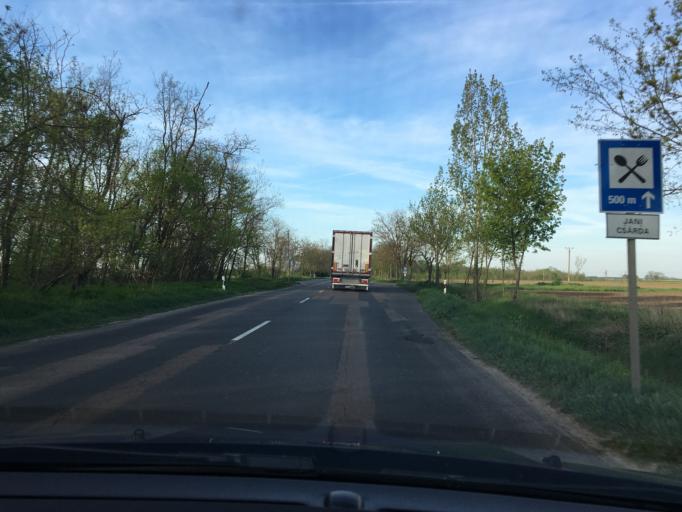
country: HU
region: Hajdu-Bihar
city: Berettyoujfalu
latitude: 47.1741
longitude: 21.5207
